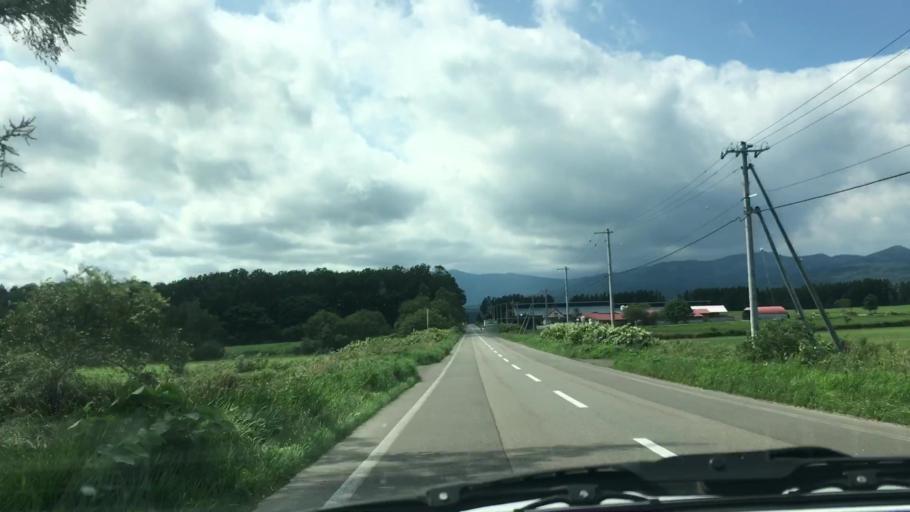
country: JP
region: Hokkaido
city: Otofuke
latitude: 43.2805
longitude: 143.3373
